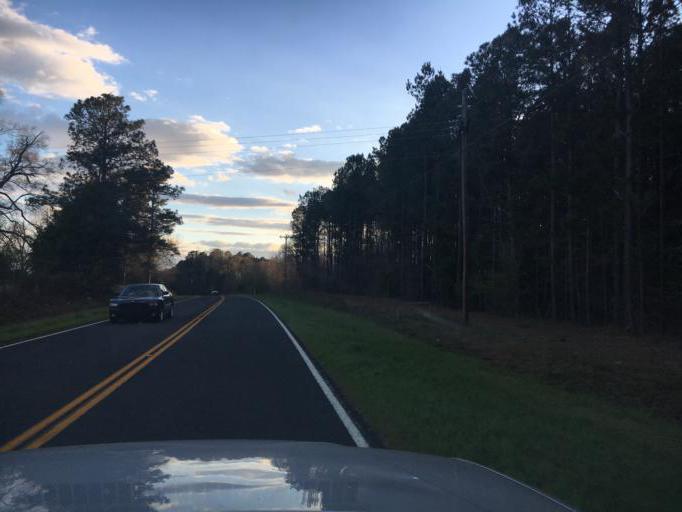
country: US
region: South Carolina
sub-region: Greenwood County
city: Greenwood
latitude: 34.1107
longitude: -82.1831
